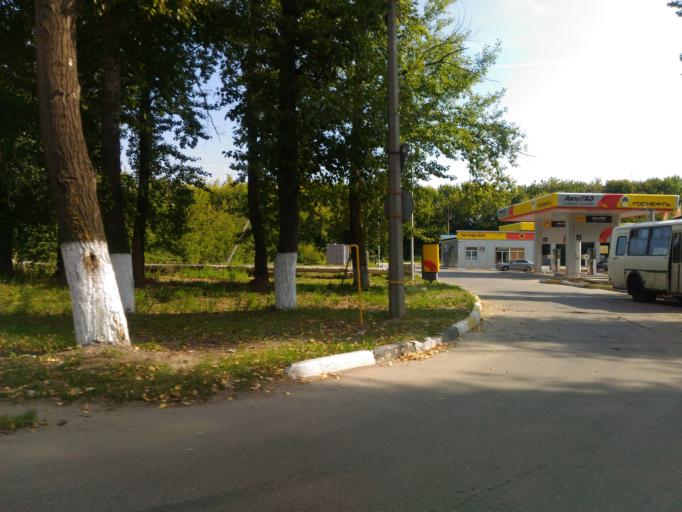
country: RU
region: Ulyanovsk
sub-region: Ulyanovskiy Rayon
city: Ulyanovsk
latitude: 54.3222
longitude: 48.4822
